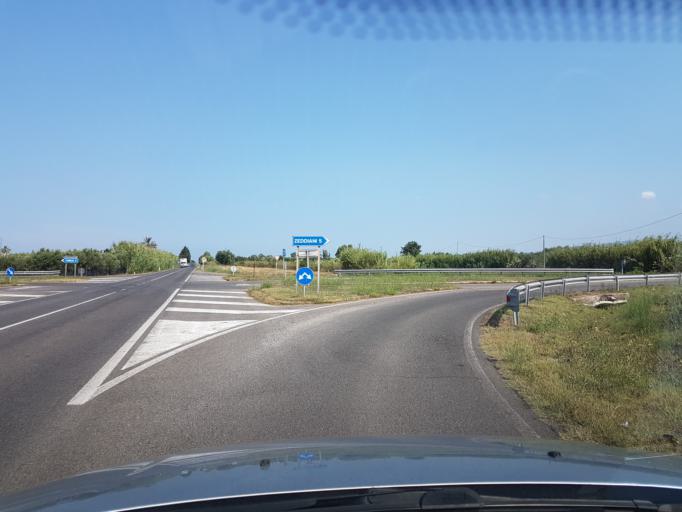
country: IT
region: Sardinia
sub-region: Provincia di Oristano
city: Donigala Fenugheddu
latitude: 39.9511
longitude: 8.5603
